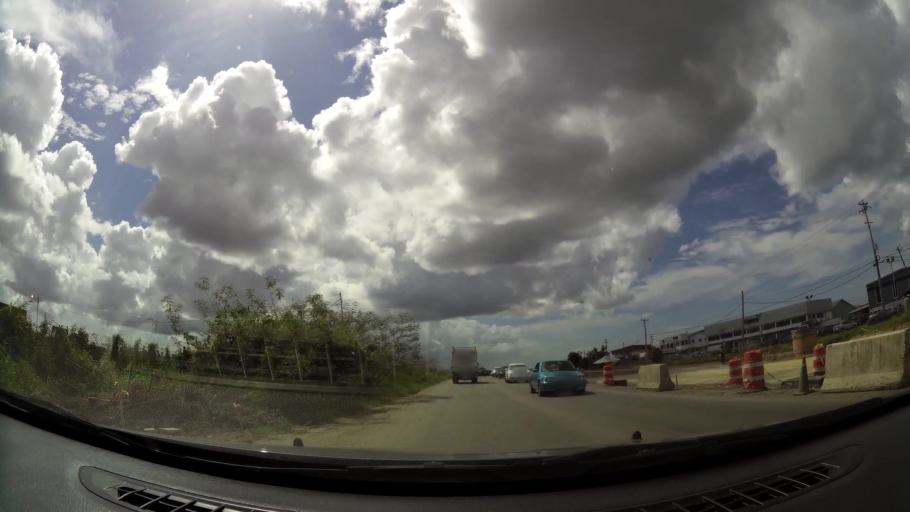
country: TT
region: City of San Fernando
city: San Fernando
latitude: 10.2478
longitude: -61.4904
